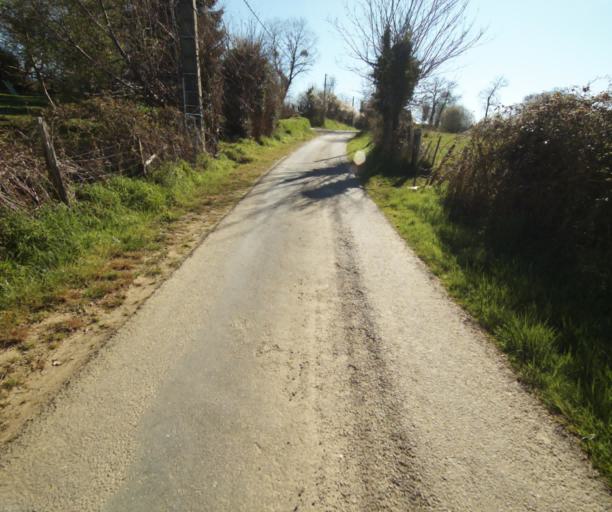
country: FR
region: Limousin
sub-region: Departement de la Correze
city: Chamboulive
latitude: 45.4059
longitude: 1.7037
